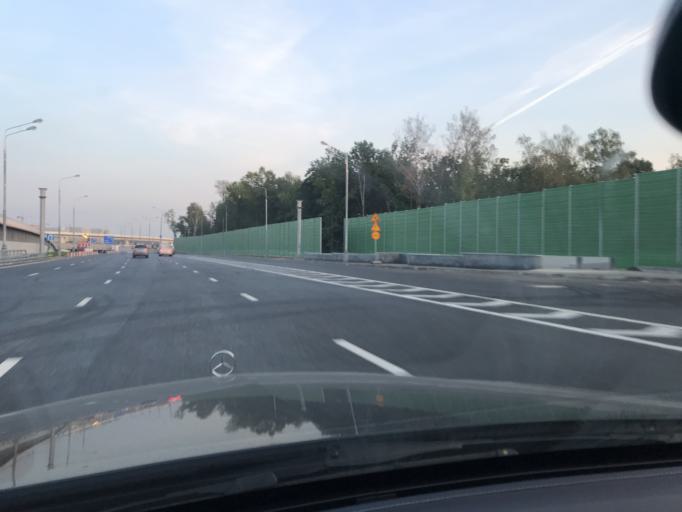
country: RU
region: Moskovskaya
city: Kommunarka
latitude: 55.5758
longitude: 37.4502
